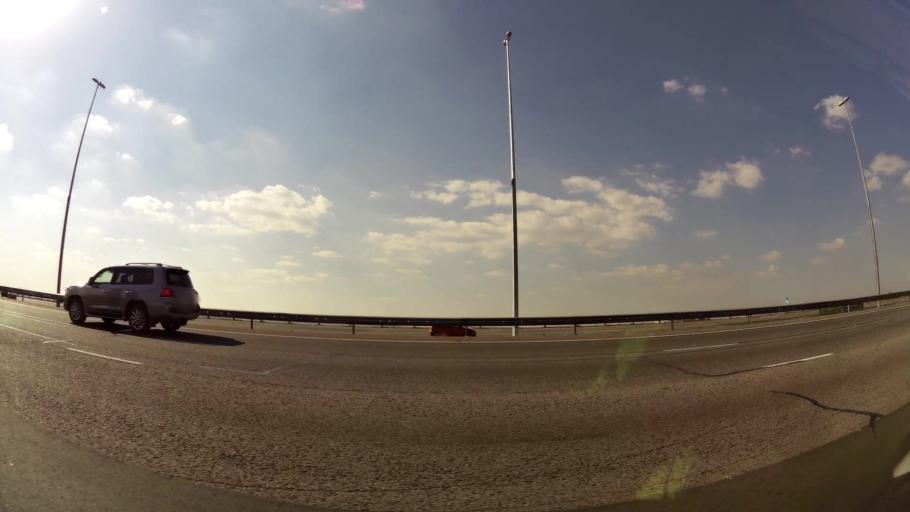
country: ZA
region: Gauteng
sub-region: Ekurhuleni Metropolitan Municipality
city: Tembisa
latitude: -26.0551
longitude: 28.2811
